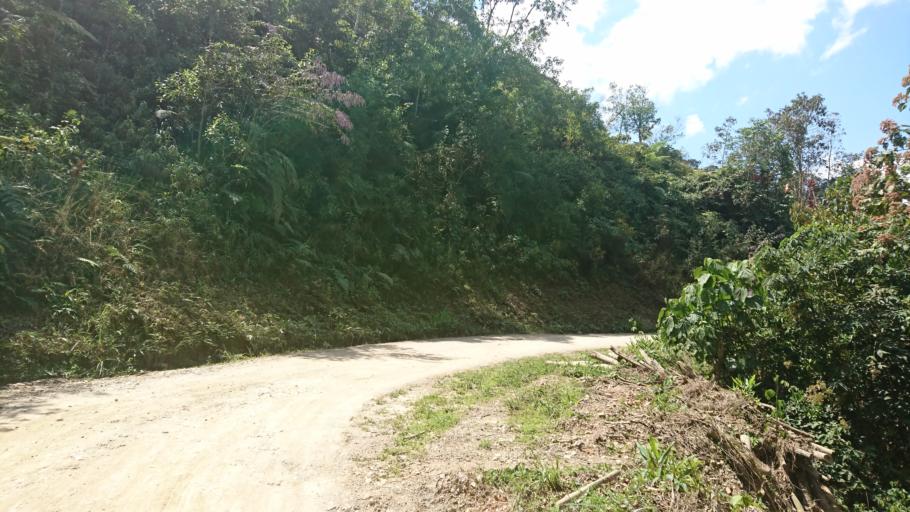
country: BO
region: La Paz
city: Coroico
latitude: -16.0983
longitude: -67.7871
